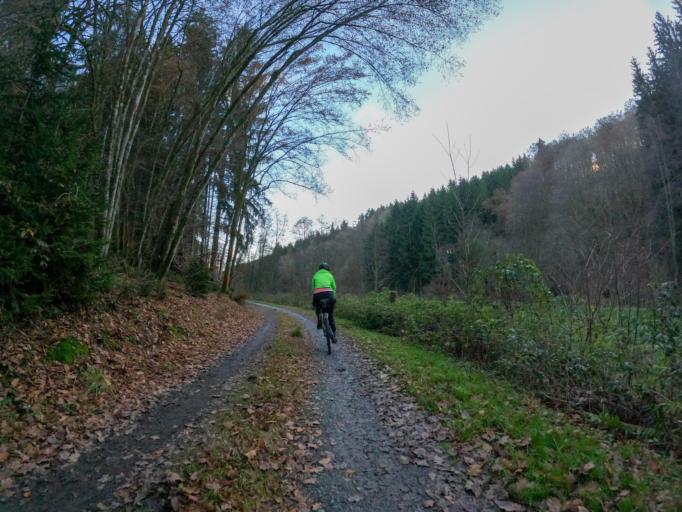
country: LU
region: Diekirch
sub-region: Canton de Wiltz
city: Bavigne
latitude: 49.9421
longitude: 5.8331
